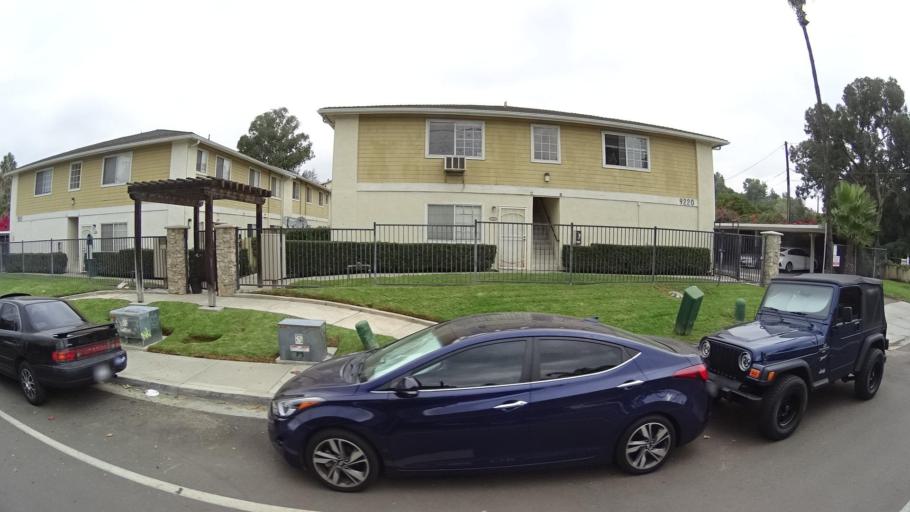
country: US
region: California
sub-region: San Diego County
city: Spring Valley
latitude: 32.7446
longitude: -116.9998
